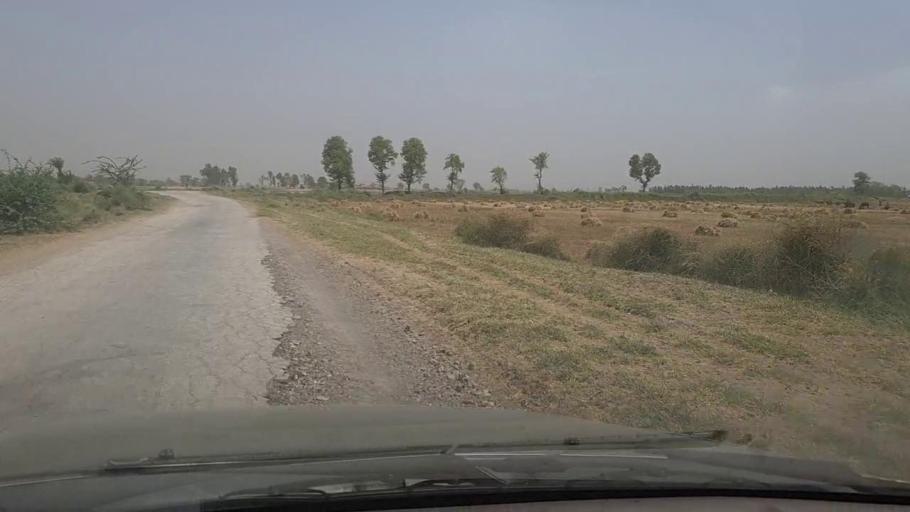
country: PK
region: Sindh
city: Madeji
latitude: 27.8160
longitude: 68.3980
